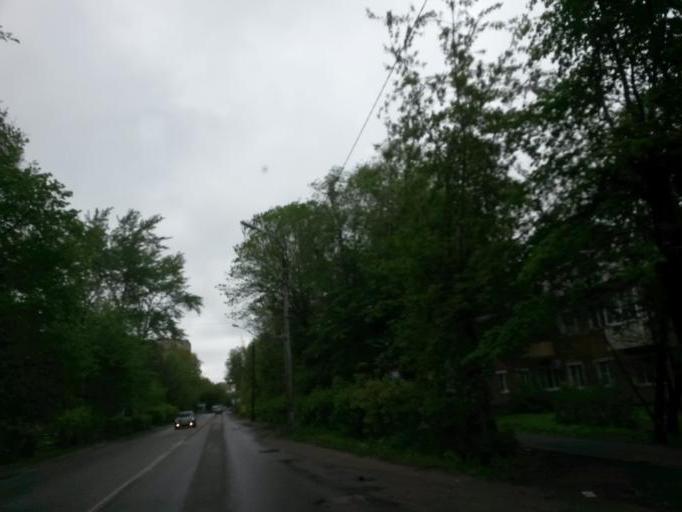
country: RU
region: Moskovskaya
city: Klimovsk
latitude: 55.3665
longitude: 37.5374
